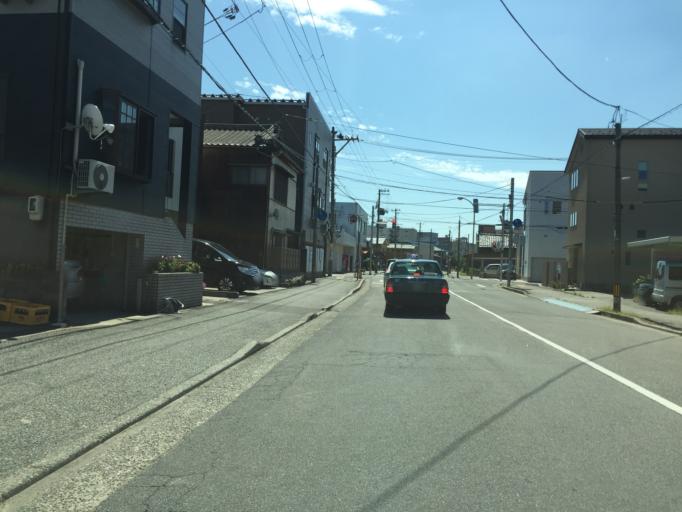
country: JP
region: Niigata
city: Niigata-shi
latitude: 37.9280
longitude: 139.0497
